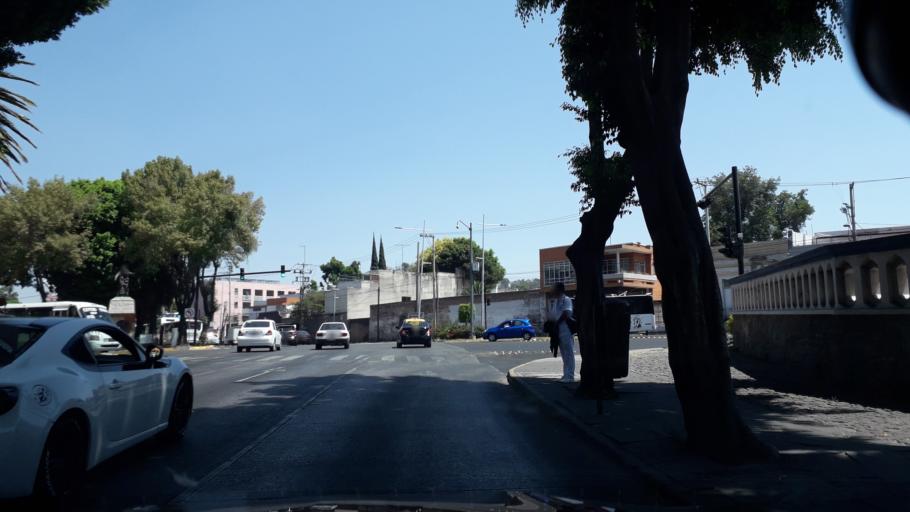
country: MX
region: Puebla
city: Puebla
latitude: 19.0484
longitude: -98.1892
